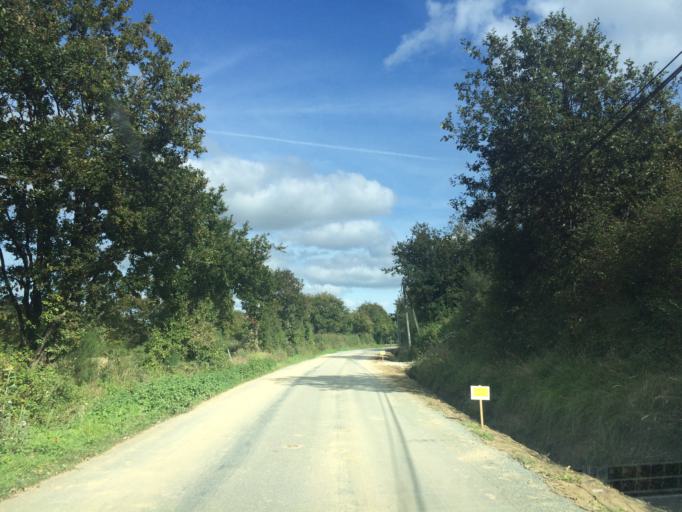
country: FR
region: Pays de la Loire
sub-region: Departement de la Loire-Atlantique
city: Chemere
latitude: 47.1013
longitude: -1.9084
